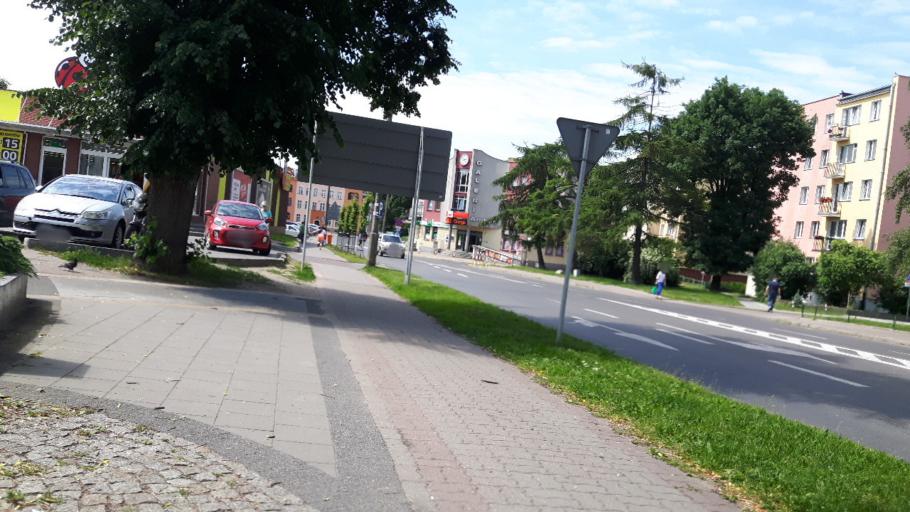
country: PL
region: Warmian-Masurian Voivodeship
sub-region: Powiat braniewski
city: Braniewo
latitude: 54.3843
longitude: 19.8276
